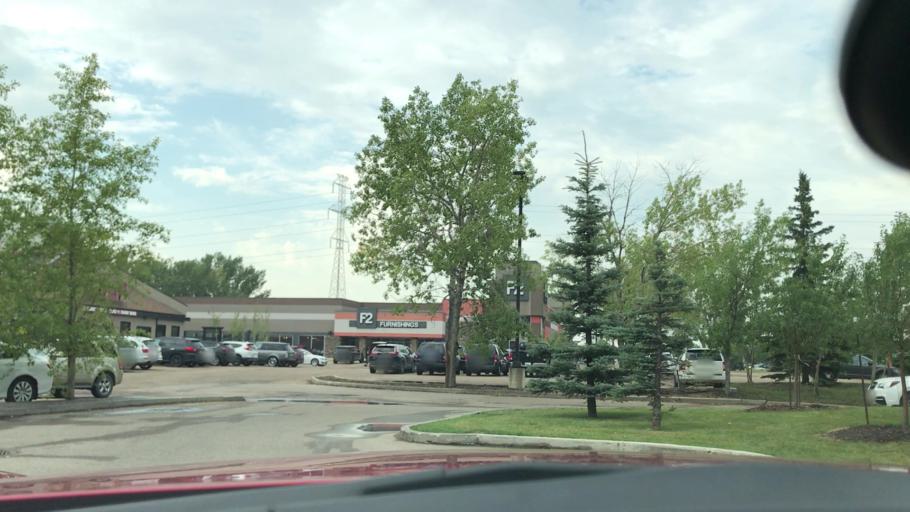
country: CA
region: Alberta
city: Edmonton
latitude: 53.4600
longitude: -113.4933
